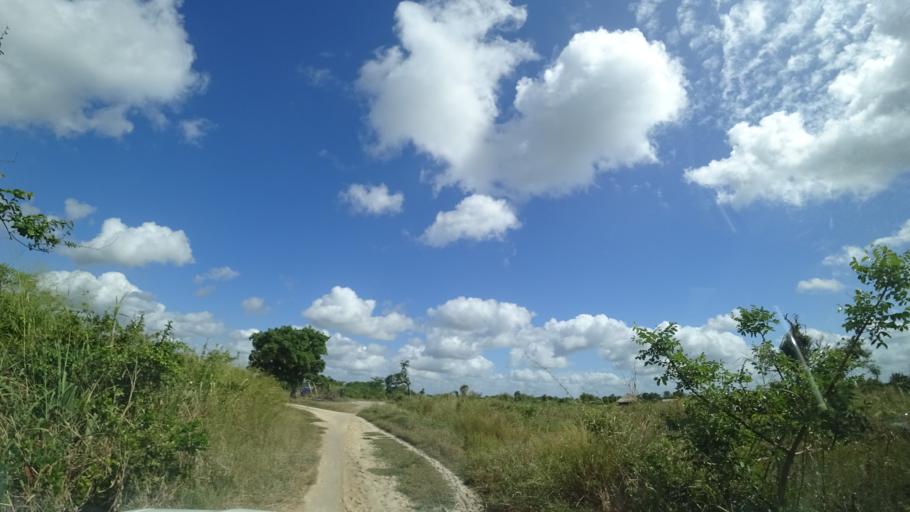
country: MZ
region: Sofala
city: Dondo
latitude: -19.3571
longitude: 34.5828
